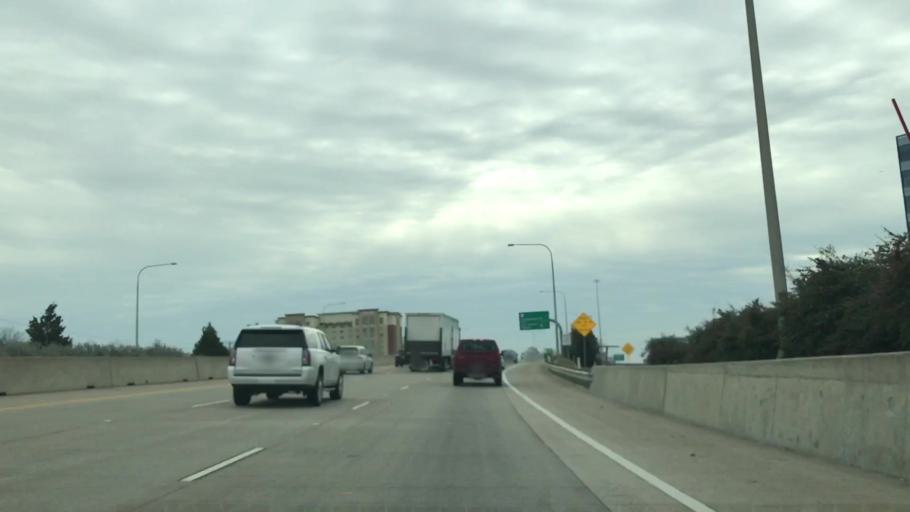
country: US
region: Texas
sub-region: Collin County
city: Frisco
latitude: 33.1052
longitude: -96.8230
